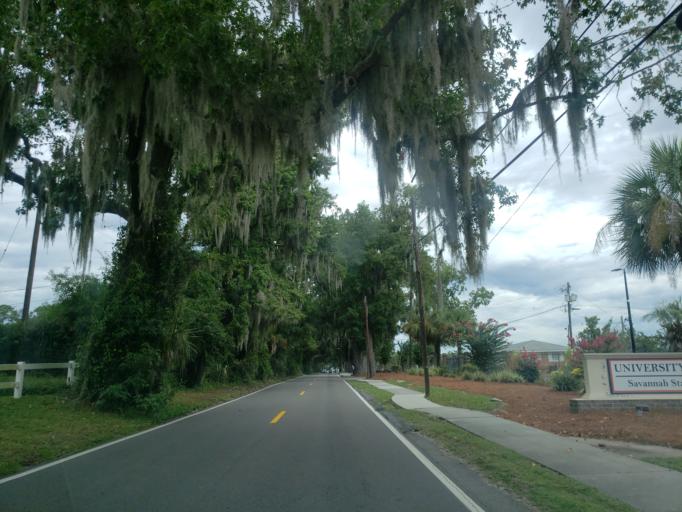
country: US
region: Georgia
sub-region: Chatham County
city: Thunderbolt
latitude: 32.0238
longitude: -81.0692
